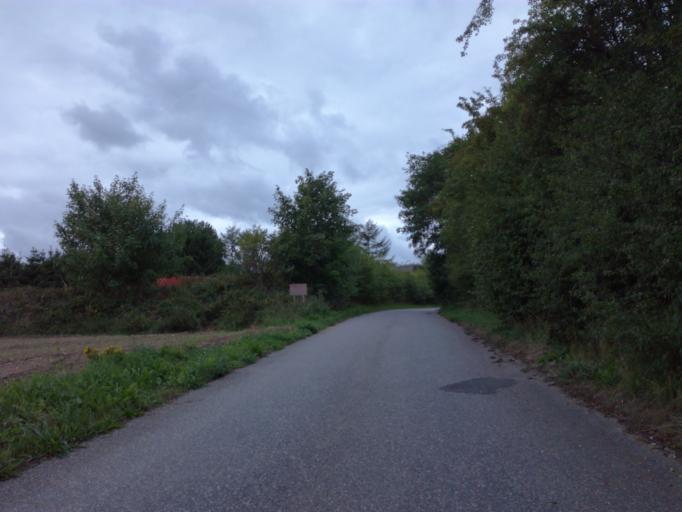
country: DK
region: South Denmark
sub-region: Vejle Kommune
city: Borkop
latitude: 55.6689
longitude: 9.5951
